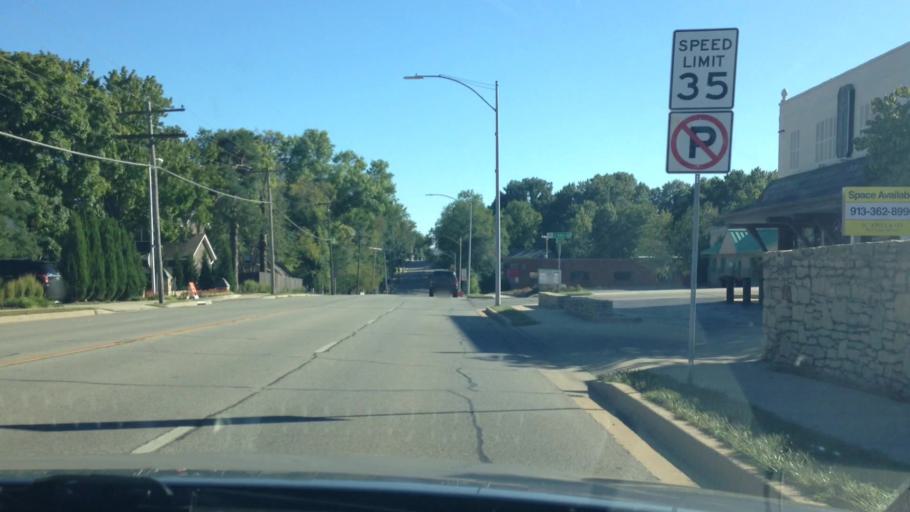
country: US
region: Kansas
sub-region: Johnson County
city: Westwood
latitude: 39.0409
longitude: -94.6120
